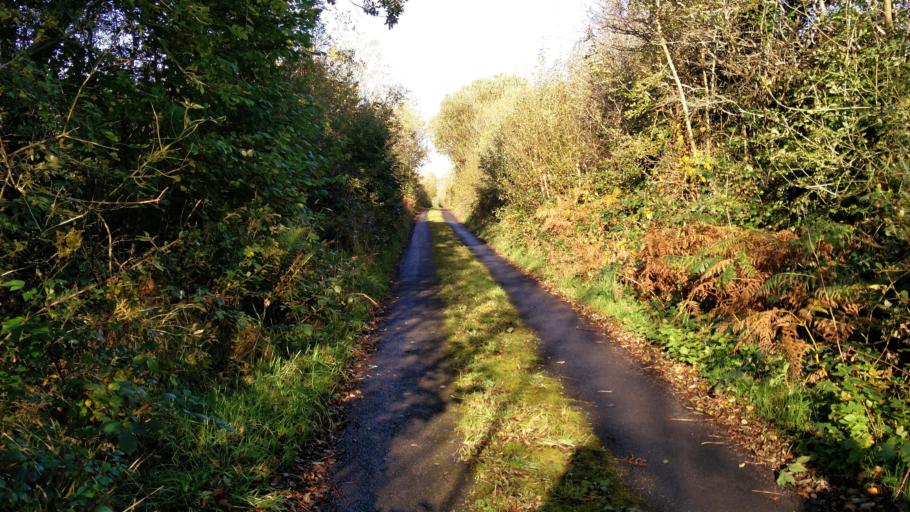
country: IE
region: Connaught
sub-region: Maigh Eo
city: Westport
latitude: 53.7811
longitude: -9.4551
